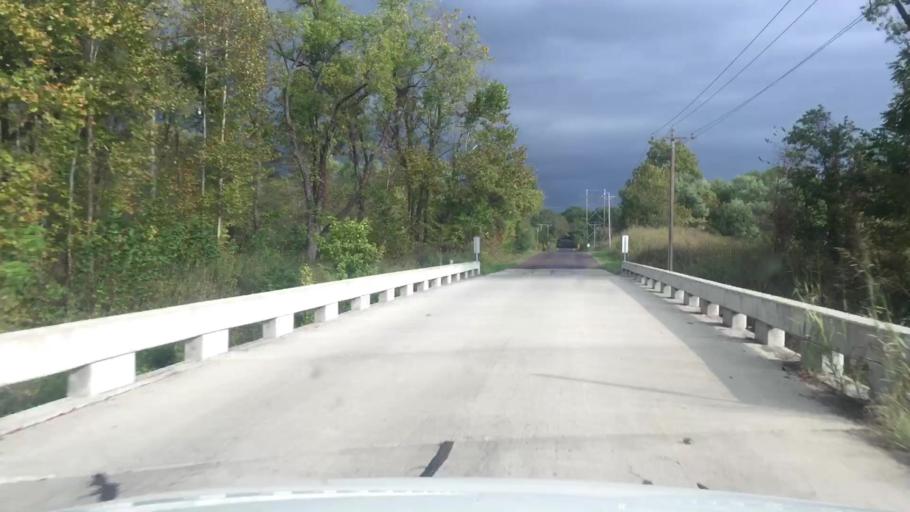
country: US
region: Missouri
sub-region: Boone County
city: Columbia
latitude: 38.8654
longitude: -92.3738
